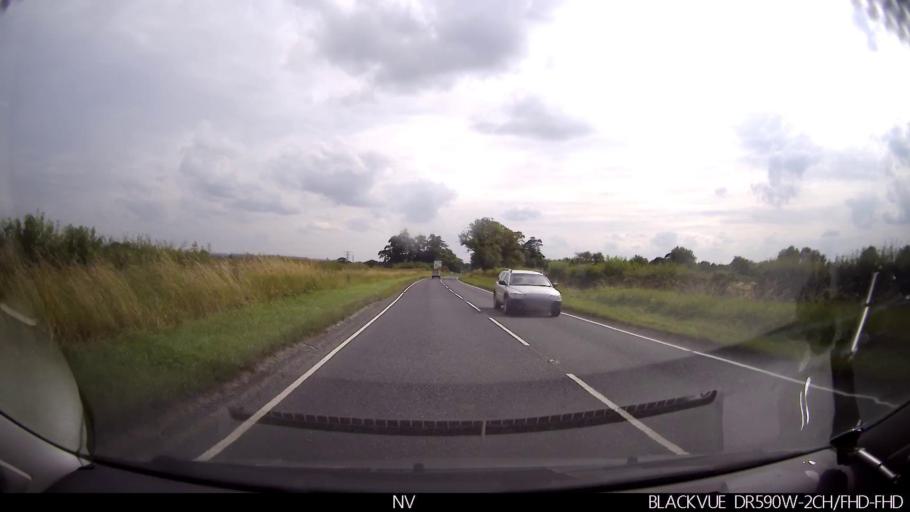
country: GB
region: England
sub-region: North Yorkshire
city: Malton
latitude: 54.1575
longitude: -0.7712
